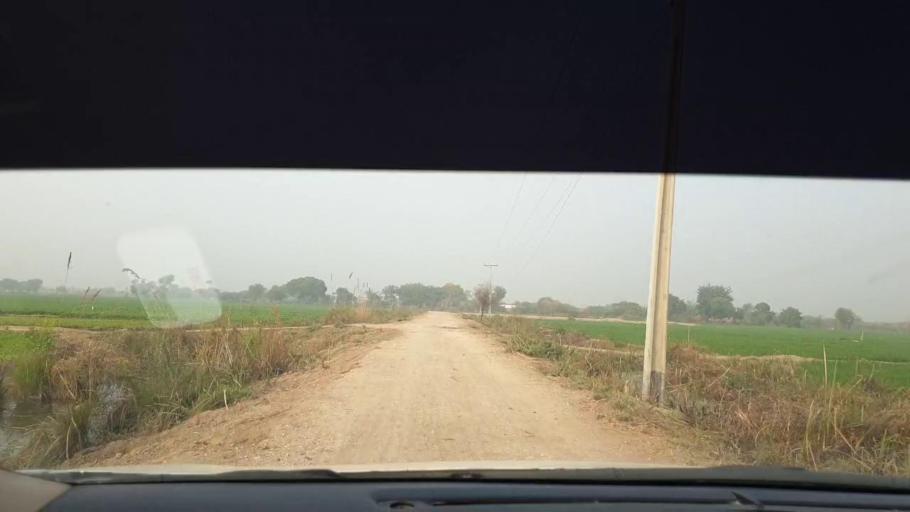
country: PK
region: Sindh
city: Berani
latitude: 25.7995
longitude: 68.8518
